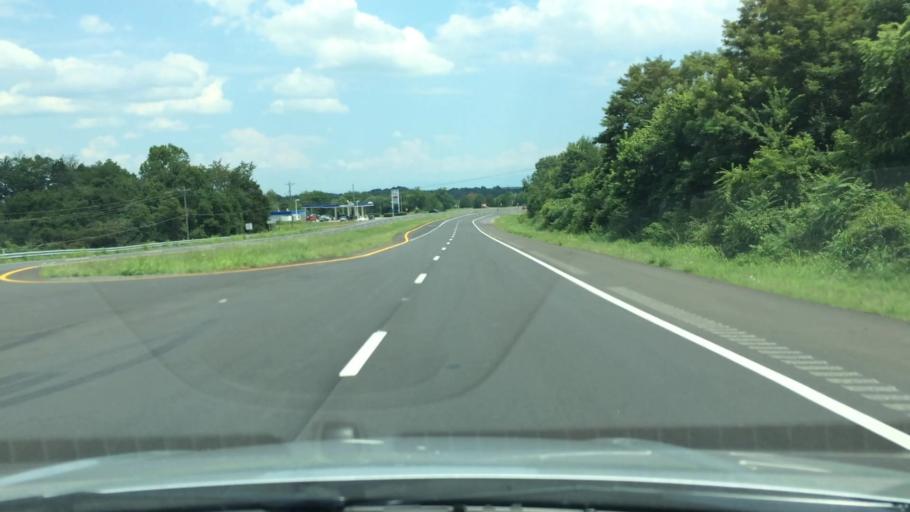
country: US
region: Tennessee
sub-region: Hamblen County
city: Morristown
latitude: 36.1701
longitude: -83.2247
